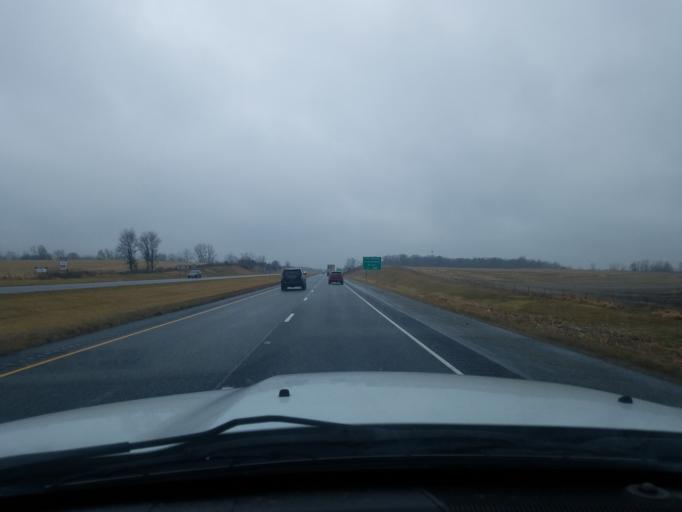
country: US
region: Indiana
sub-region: Huntington County
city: Roanoke
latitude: 41.0035
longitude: -85.2617
